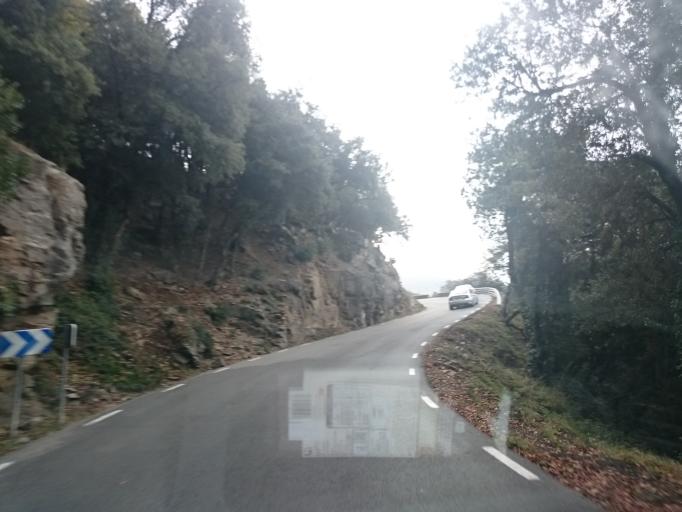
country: ES
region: Catalonia
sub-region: Provincia de Barcelona
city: Fogars de Montclus
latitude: 41.7577
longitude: 2.4687
